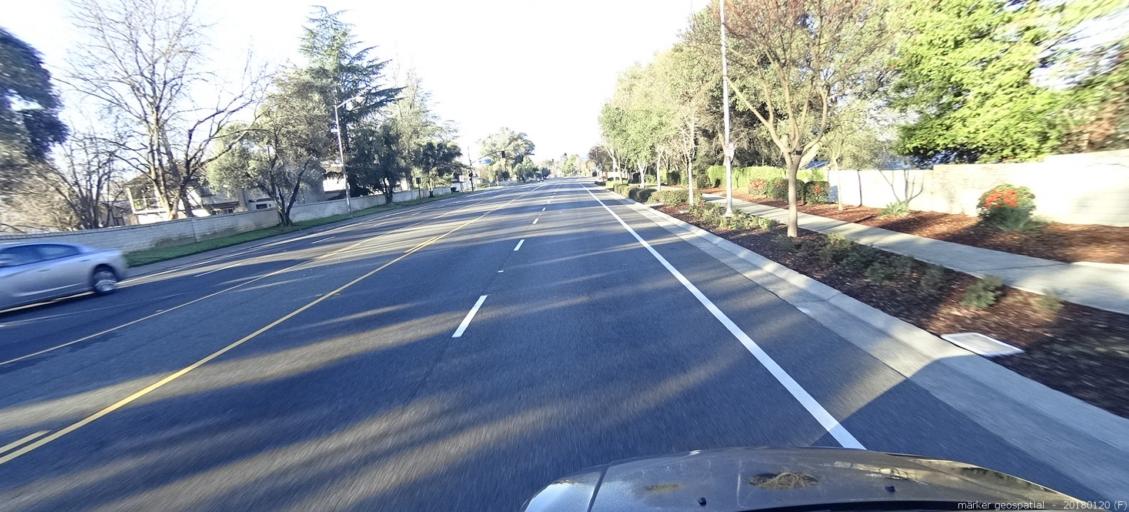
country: US
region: California
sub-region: Sacramento County
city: Fair Oaks
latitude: 38.6172
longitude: -121.2768
